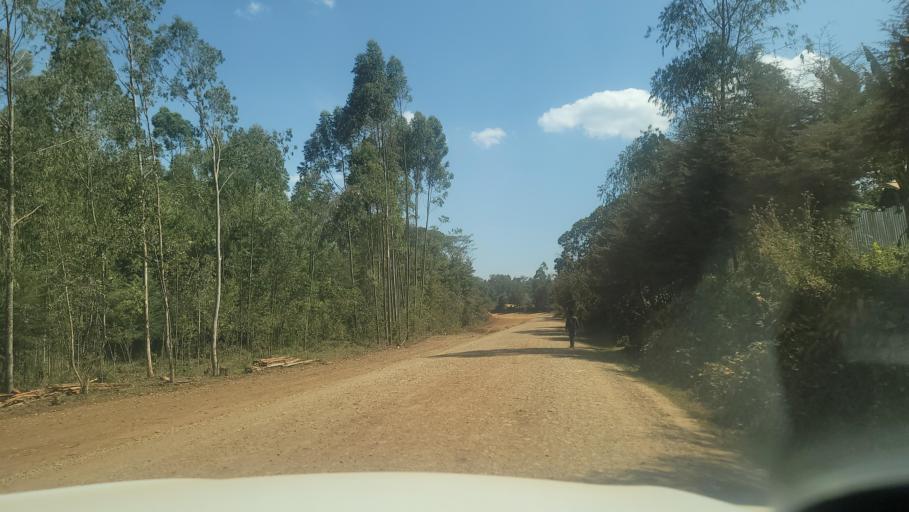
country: ET
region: Oromiya
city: Agaro
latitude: 7.7866
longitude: 36.4057
